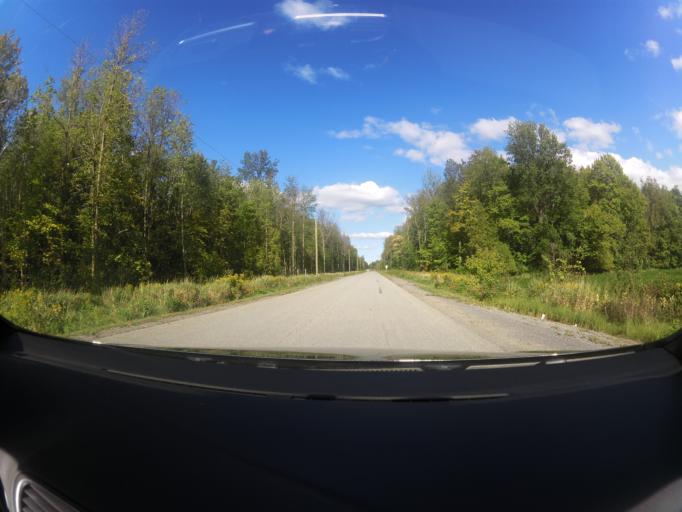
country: CA
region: Ontario
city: Carleton Place
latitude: 45.1336
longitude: -76.0909
